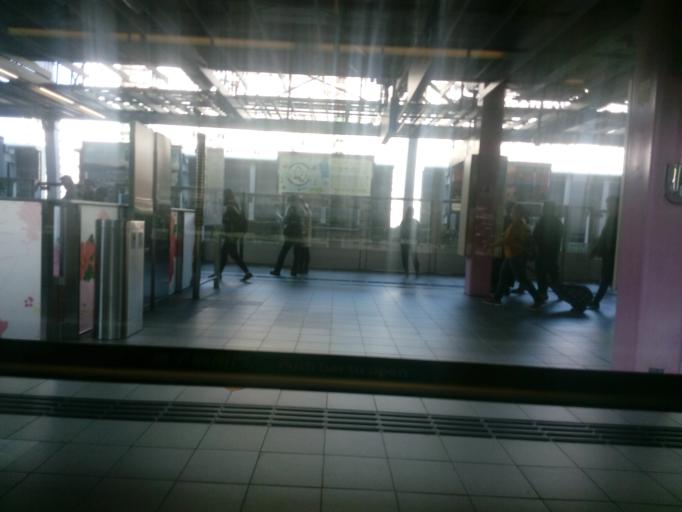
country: HK
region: Sha Tin
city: Sha Tin
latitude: 22.3770
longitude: 114.1948
